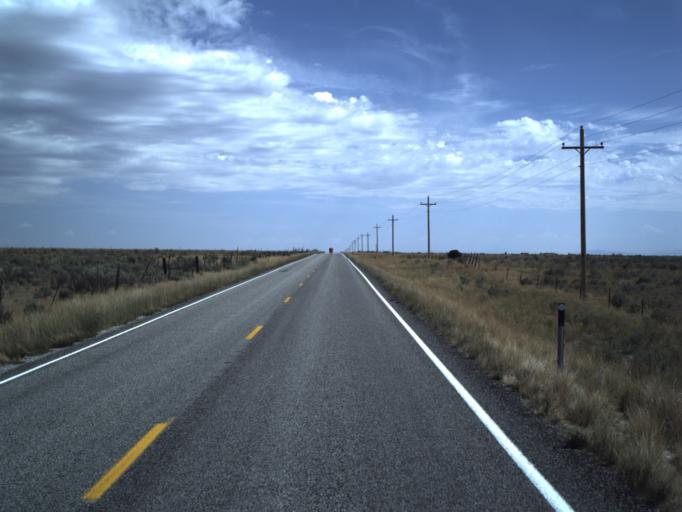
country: US
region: Idaho
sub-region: Cassia County
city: Burley
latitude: 41.8171
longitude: -113.2973
